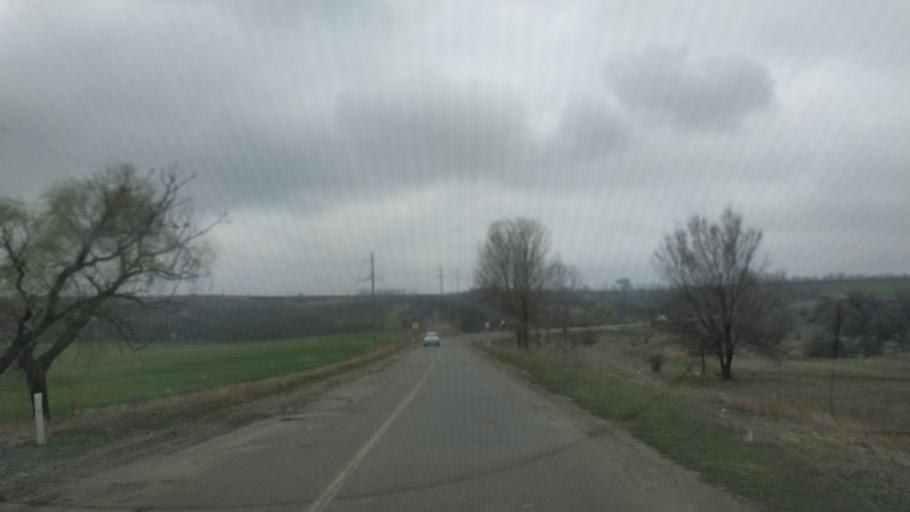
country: MD
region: Gagauzia
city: Bugeac
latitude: 46.3349
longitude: 28.7576
